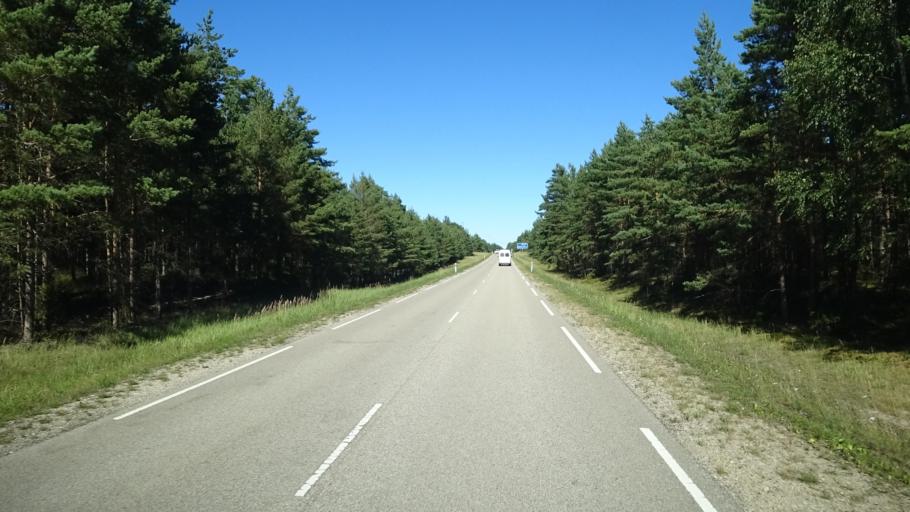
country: LV
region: Dundaga
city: Dundaga
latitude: 57.7520
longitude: 22.5838
